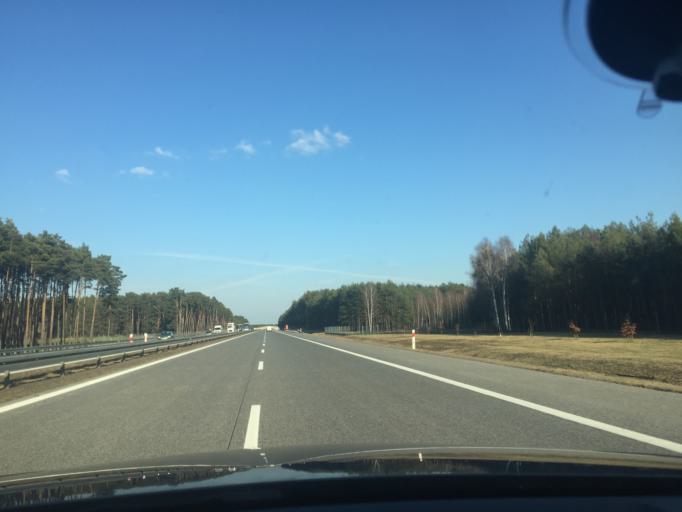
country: PL
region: Lubusz
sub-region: Powiat swiebodzinski
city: Zbaszynek
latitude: 52.3183
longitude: 15.8000
